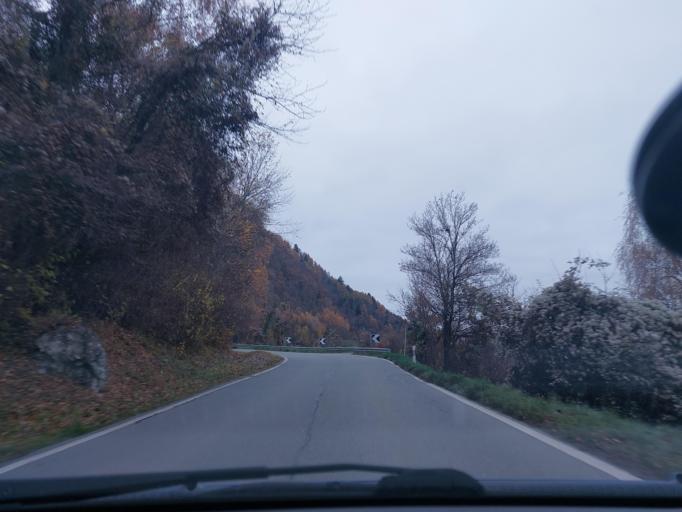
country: CH
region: Valais
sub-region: Conthey District
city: Basse-Nendaz
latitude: 46.2032
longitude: 7.3117
